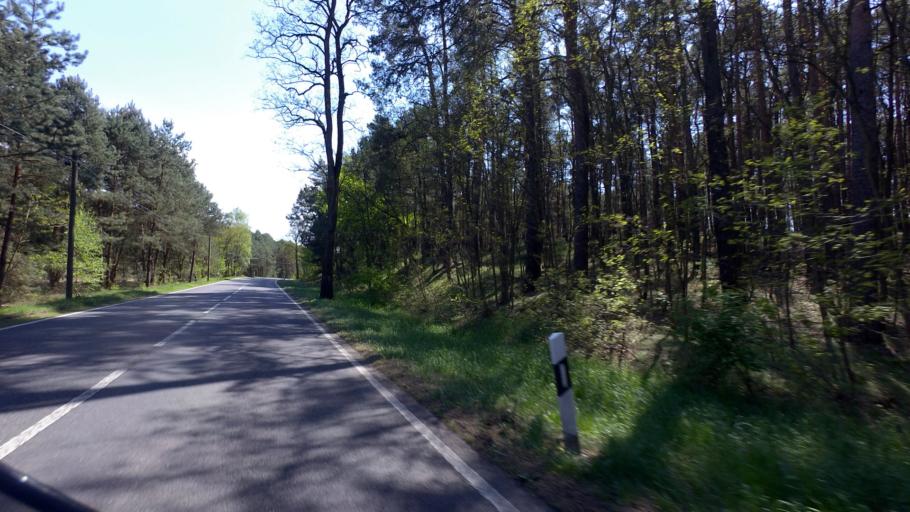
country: DE
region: Brandenburg
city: Lieberose
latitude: 52.0007
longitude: 14.1998
